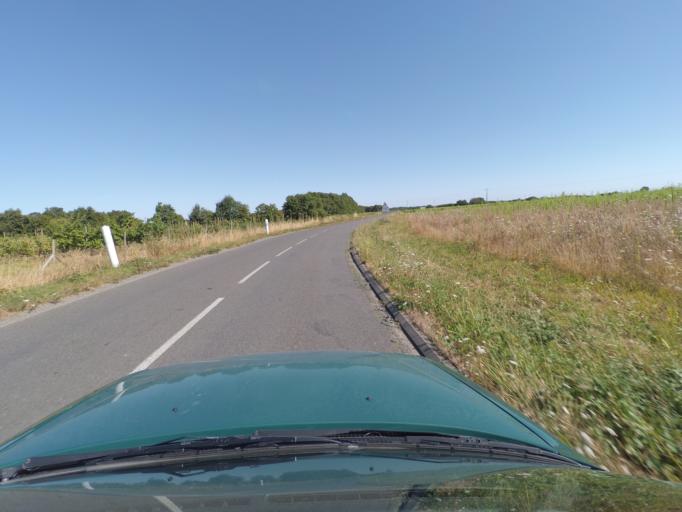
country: FR
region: Pays de la Loire
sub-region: Departement de la Loire-Atlantique
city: Maisdon-sur-Sevre
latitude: 47.1023
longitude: -1.3972
